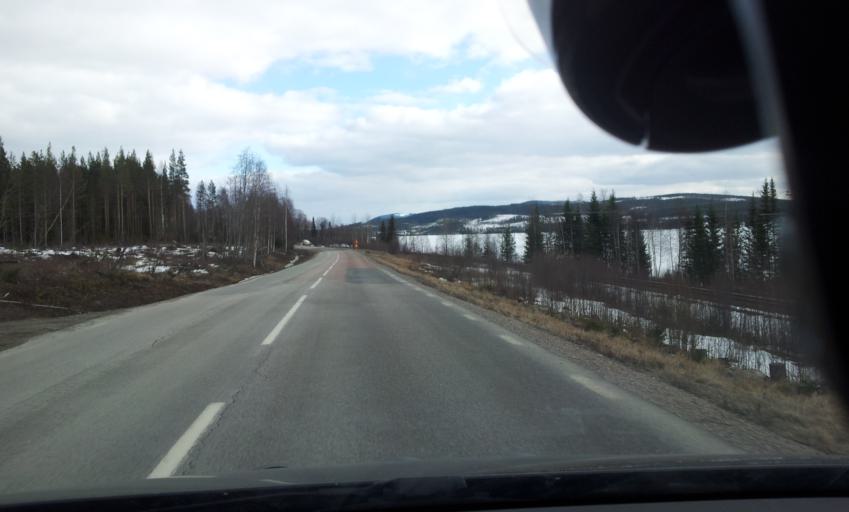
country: SE
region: Gaevleborg
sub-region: Ljusdals Kommun
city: Farila
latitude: 62.1342
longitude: 15.6948
